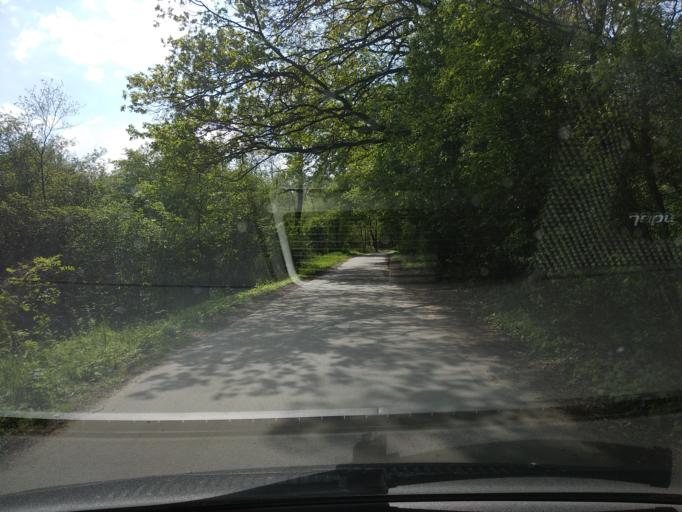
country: PL
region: Lower Silesian Voivodeship
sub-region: Powiat trzebnicki
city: Psary
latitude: 51.1583
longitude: 17.0783
